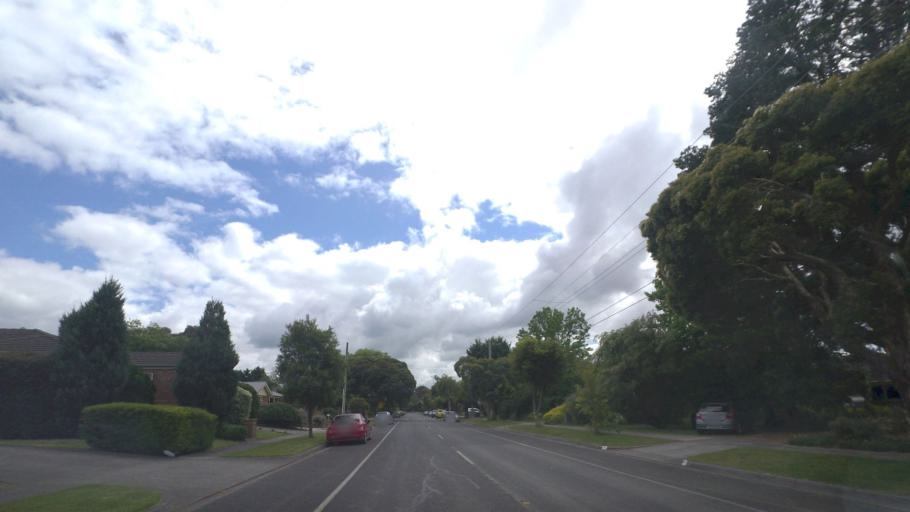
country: AU
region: Victoria
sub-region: Maroondah
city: Croydon North
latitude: -37.7896
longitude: 145.2858
